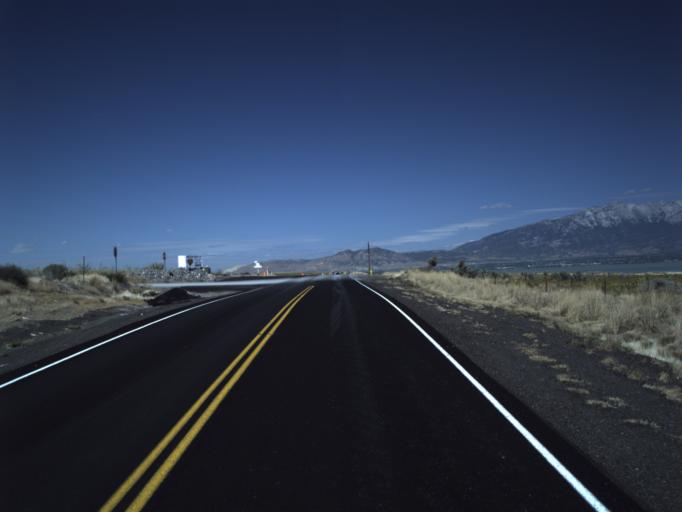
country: US
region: Utah
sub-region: Utah County
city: Saratoga Springs
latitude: 40.2617
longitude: -111.8671
